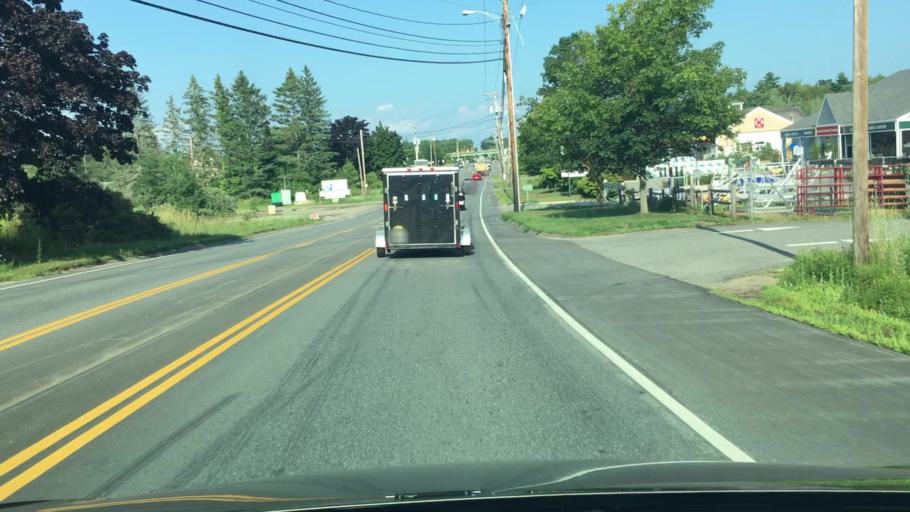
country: US
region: Maine
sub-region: Waldo County
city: Belfast
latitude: 44.4228
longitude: -69.0285
